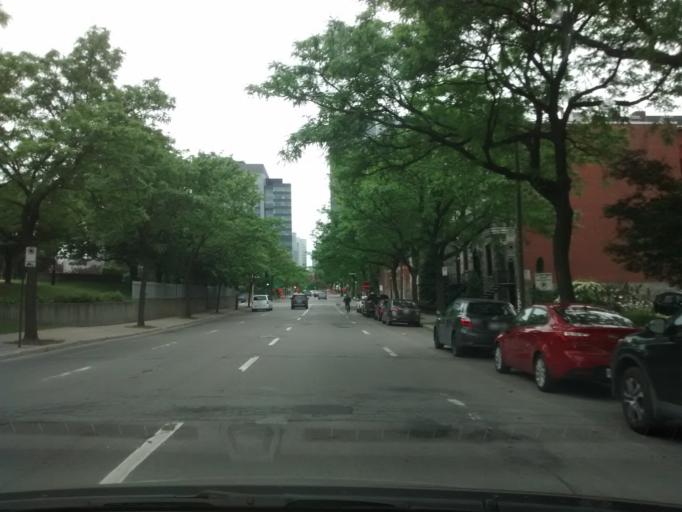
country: CA
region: Quebec
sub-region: Montreal
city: Montreal
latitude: 45.5142
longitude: -73.5535
